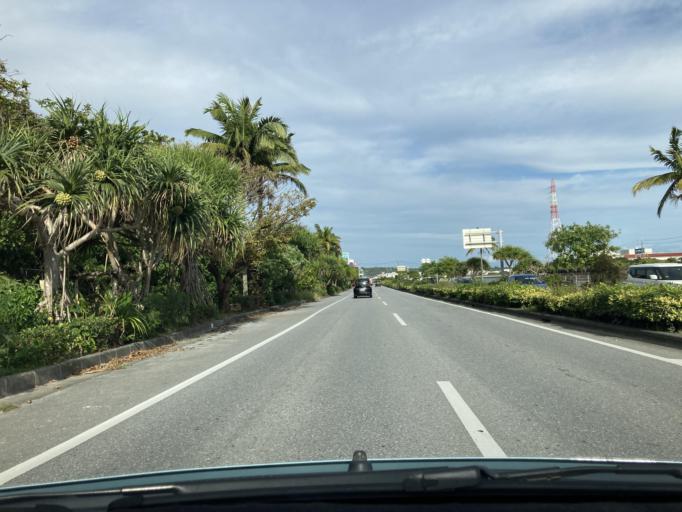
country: JP
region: Okinawa
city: Katsuren-haebaru
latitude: 26.3331
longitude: 127.8398
